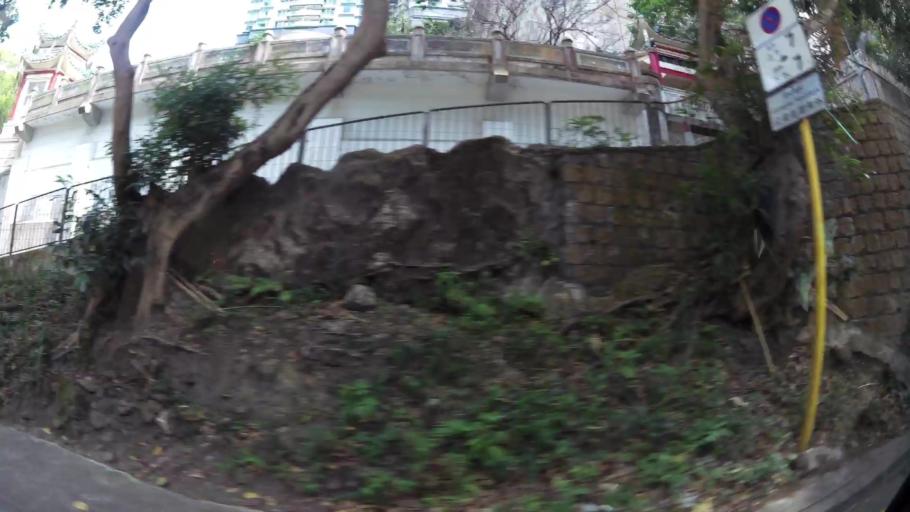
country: HK
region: Wanchai
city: Wan Chai
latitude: 22.2757
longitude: 114.1952
